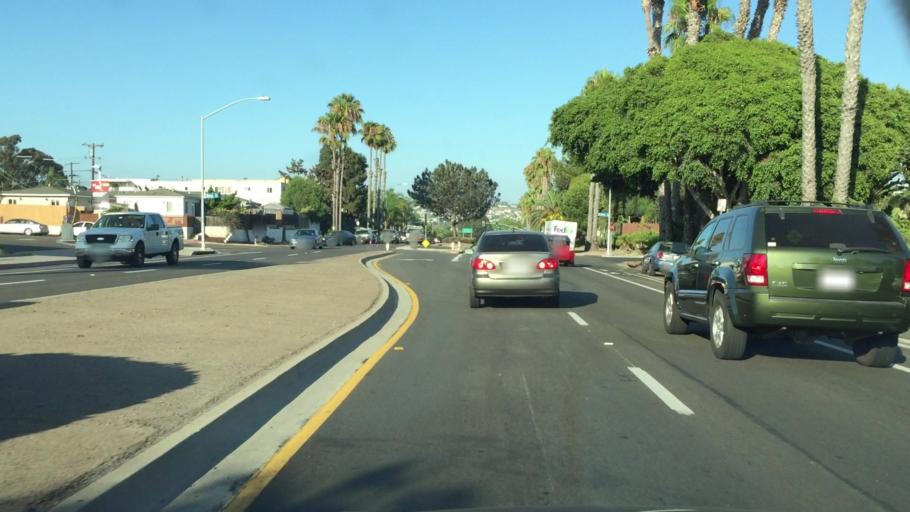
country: US
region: California
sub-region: San Diego County
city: La Jolla
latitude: 32.7997
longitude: -117.2318
